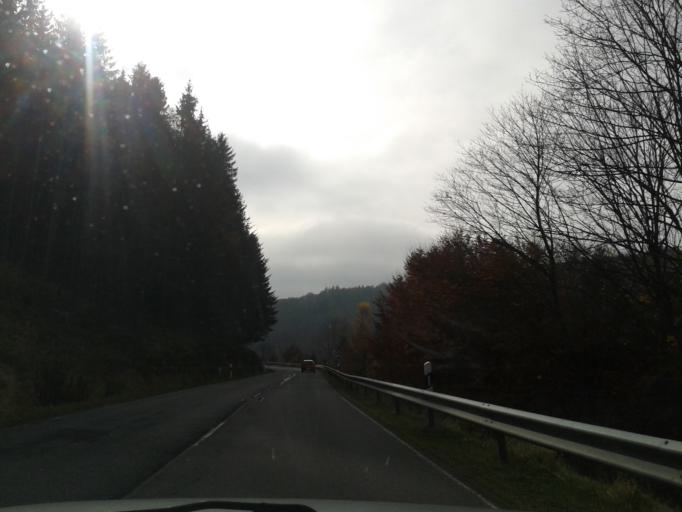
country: DE
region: North Rhine-Westphalia
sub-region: Regierungsbezirk Arnsberg
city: Bad Berleburg
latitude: 51.1159
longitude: 8.4323
